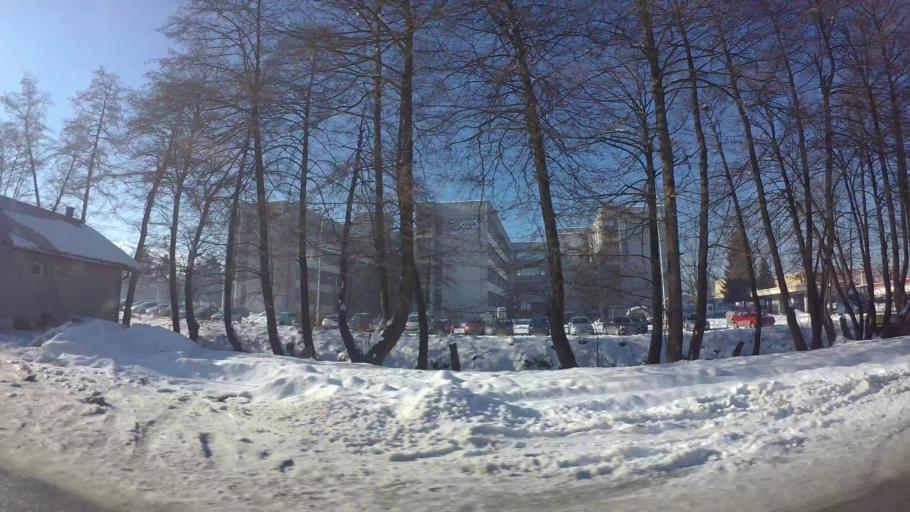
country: BA
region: Federation of Bosnia and Herzegovina
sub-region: Kanton Sarajevo
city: Sarajevo
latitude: 43.8244
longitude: 18.3754
